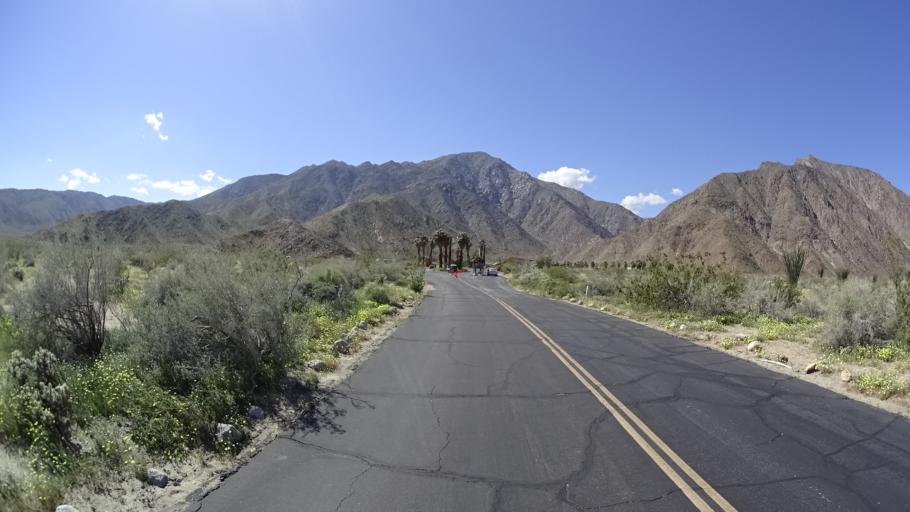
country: US
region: California
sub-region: San Diego County
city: Borrego Springs
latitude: 33.2685
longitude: -116.4045
